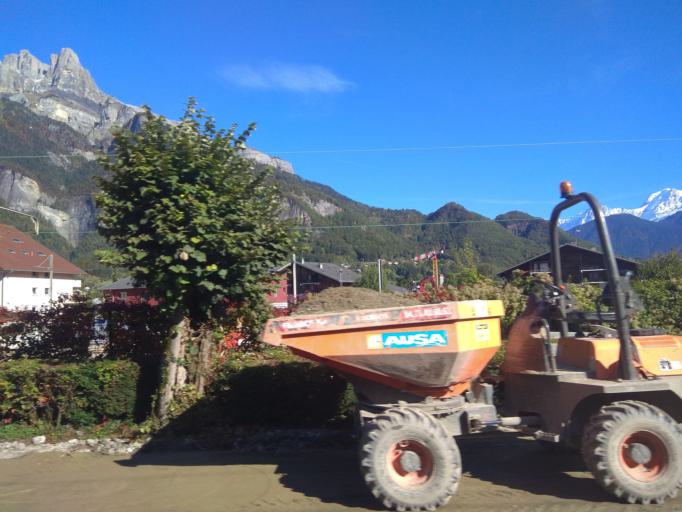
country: FR
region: Rhone-Alpes
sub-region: Departement de la Haute-Savoie
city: Sallanches
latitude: 45.9352
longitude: 6.6365
